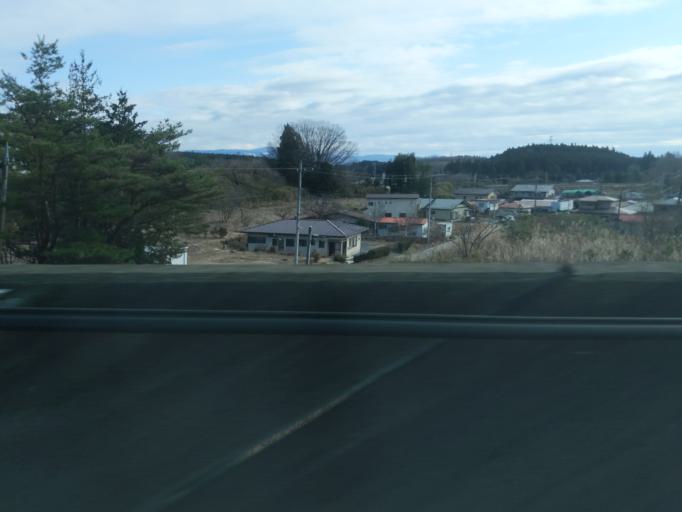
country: JP
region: Tochigi
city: Kuroiso
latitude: 37.0009
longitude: 140.0859
